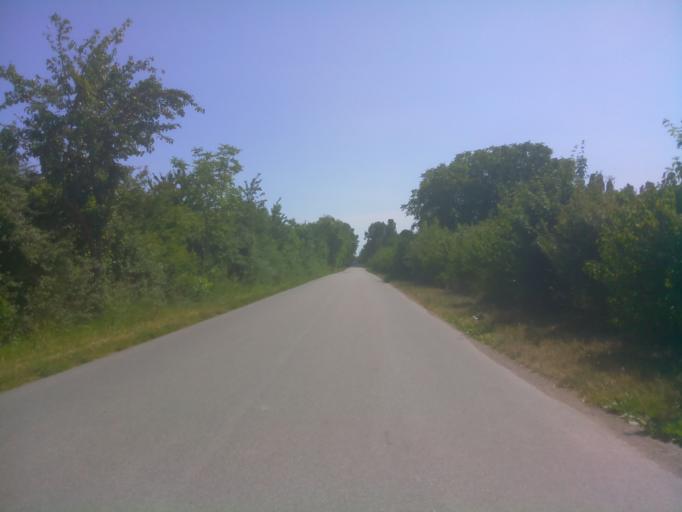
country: DE
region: Hesse
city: Viernheim
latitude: 49.5532
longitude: 8.6093
